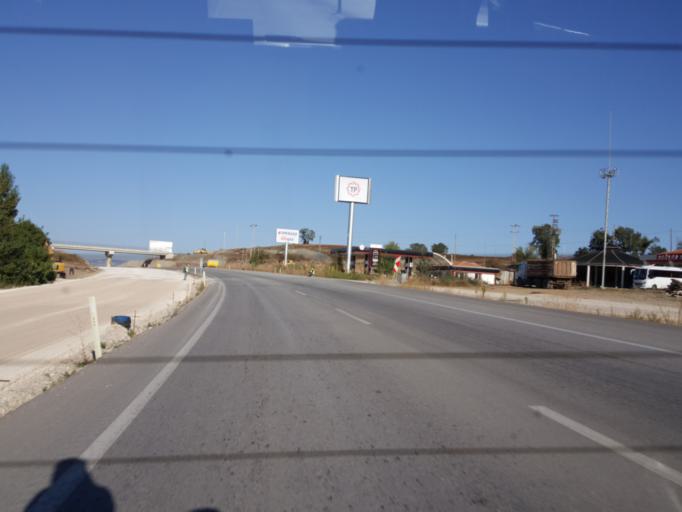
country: TR
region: Amasya
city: Ezinepazari
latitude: 40.5502
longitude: 36.1487
